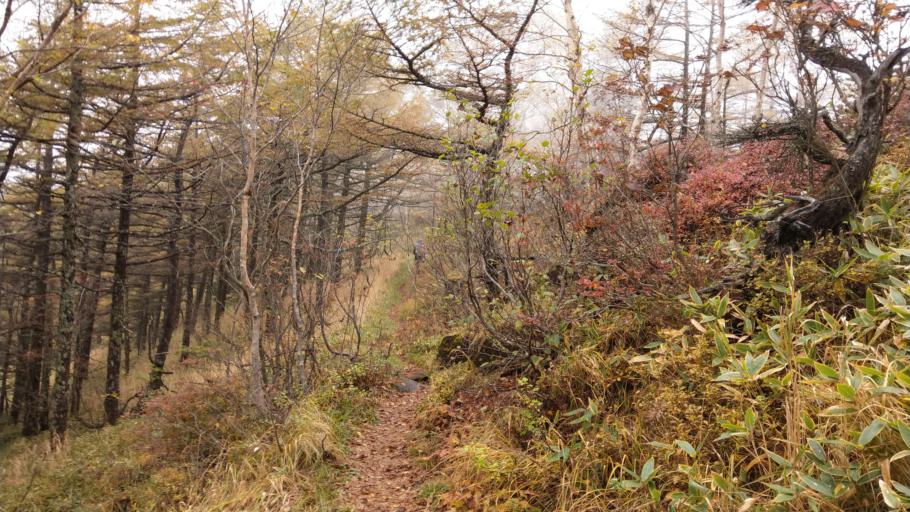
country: JP
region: Nagano
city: Komoro
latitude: 36.4043
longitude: 138.4642
